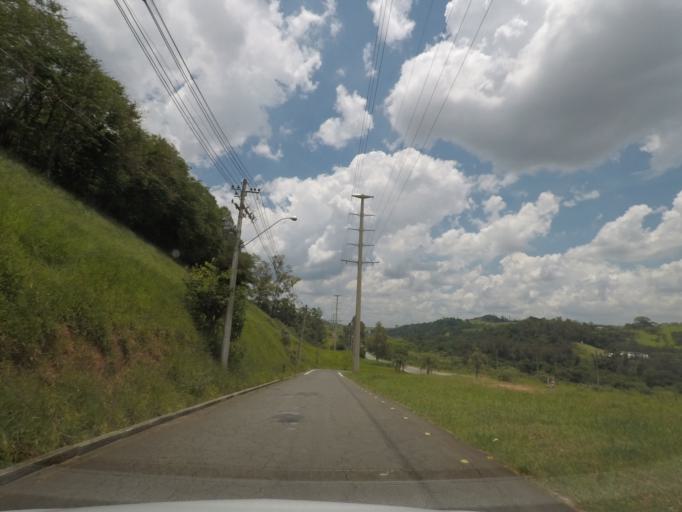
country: BR
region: Sao Paulo
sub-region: Vinhedo
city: Vinhedo
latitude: -23.0610
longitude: -47.0057
